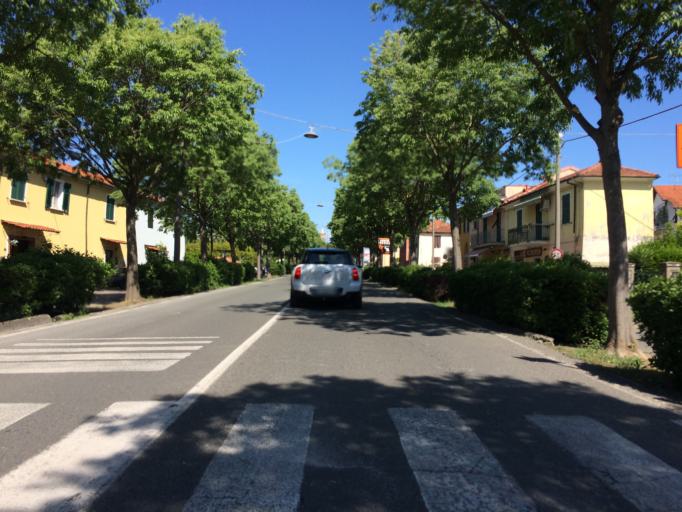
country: IT
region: Liguria
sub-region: Provincia di La Spezia
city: Sarzana
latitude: 44.1085
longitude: 9.9678
